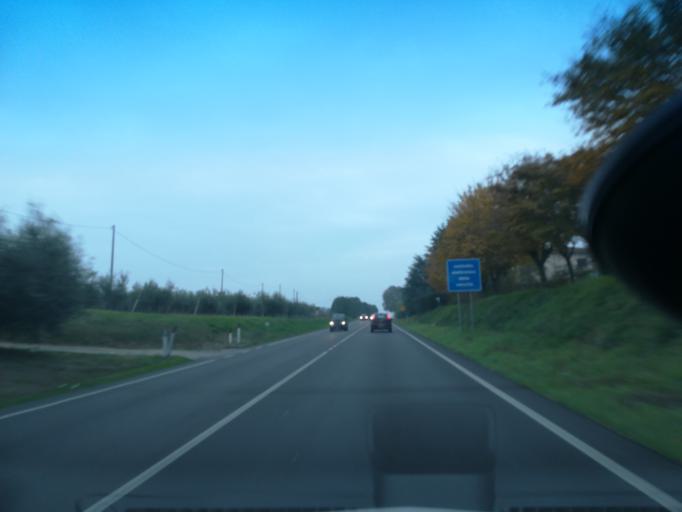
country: IT
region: Emilia-Romagna
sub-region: Provincia di Bologna
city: Imola
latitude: 44.3389
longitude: 11.7509
